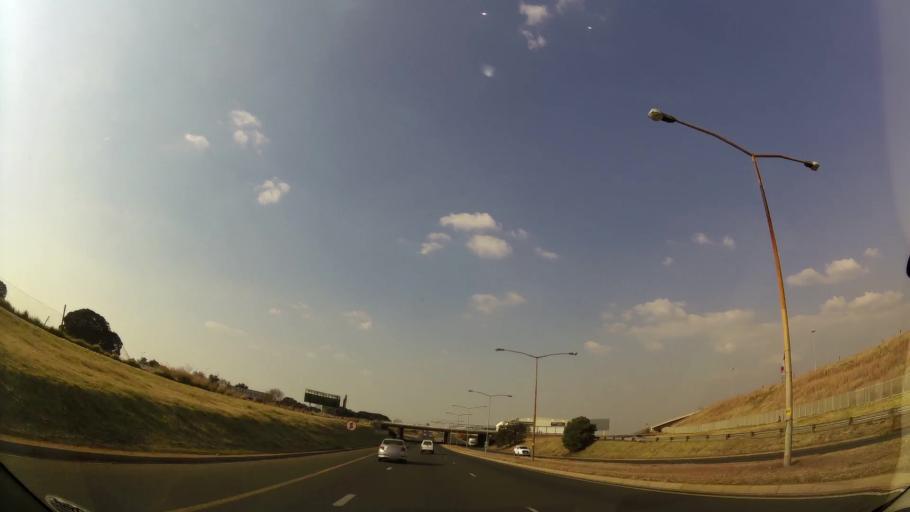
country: ZA
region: Gauteng
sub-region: City of Johannesburg Metropolitan Municipality
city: Modderfontein
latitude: -26.1006
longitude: 28.2510
